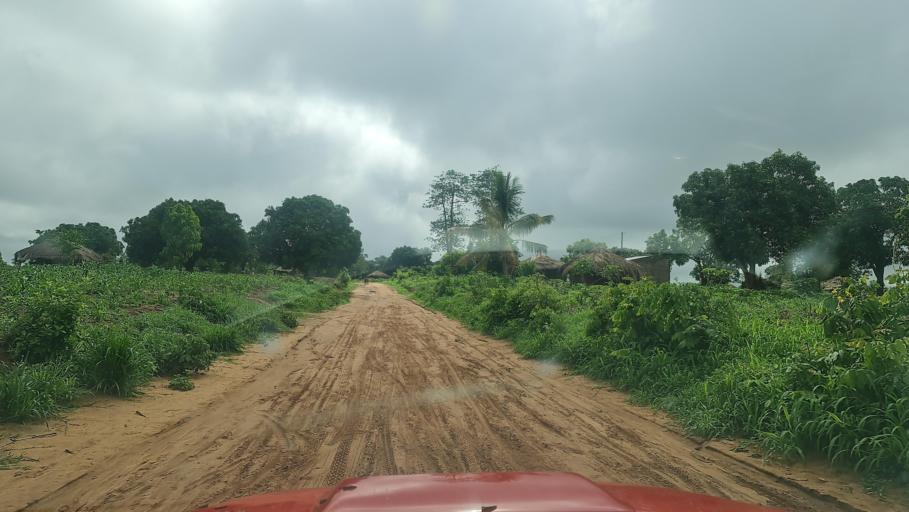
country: MW
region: Southern Region
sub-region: Nsanje District
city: Nsanje
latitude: -17.2033
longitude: 35.6942
